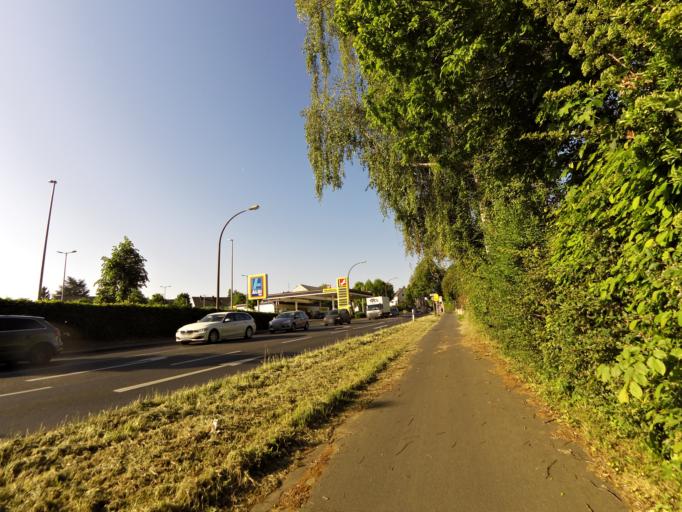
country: DE
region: North Rhine-Westphalia
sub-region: Regierungsbezirk Koln
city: Bonn
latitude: 50.6839
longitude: 7.0760
